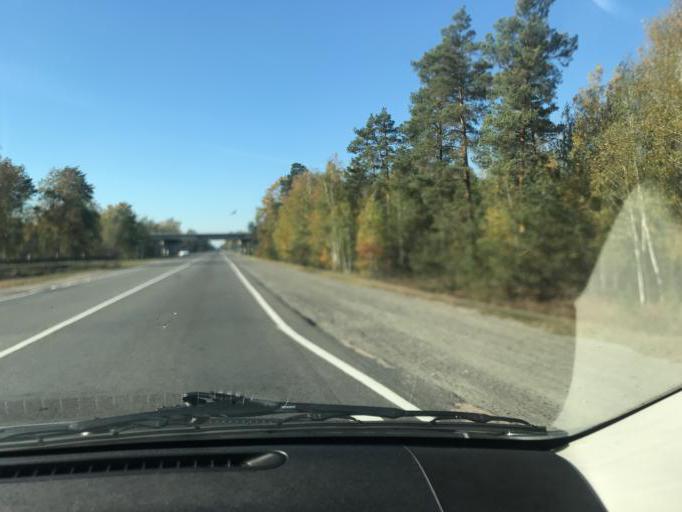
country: BY
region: Brest
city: Mikashevichy
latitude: 52.2434
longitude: 27.4483
